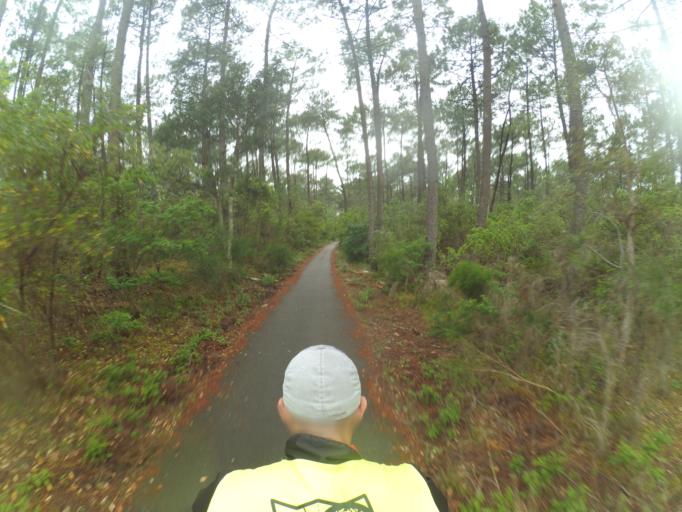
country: FR
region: Aquitaine
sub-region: Departement des Landes
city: Mimizan
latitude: 44.2194
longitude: -1.2444
